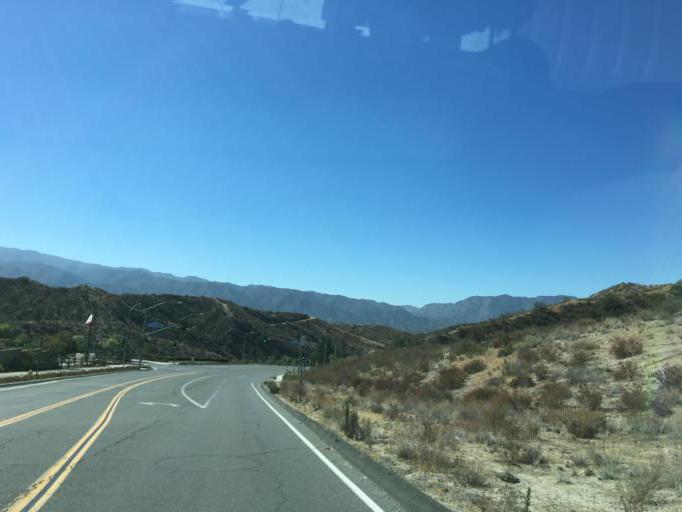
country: US
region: California
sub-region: Los Angeles County
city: Agua Dulce
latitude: 34.4397
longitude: -118.4185
